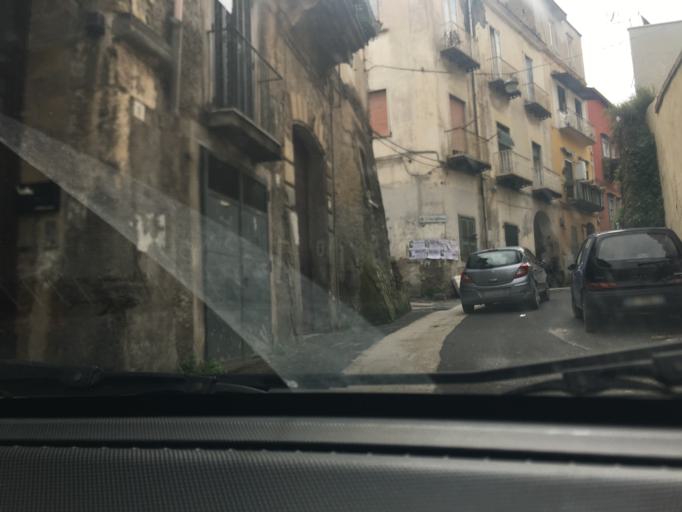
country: IT
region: Campania
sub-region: Provincia di Napoli
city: Calvizzano
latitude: 40.8961
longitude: 14.1902
